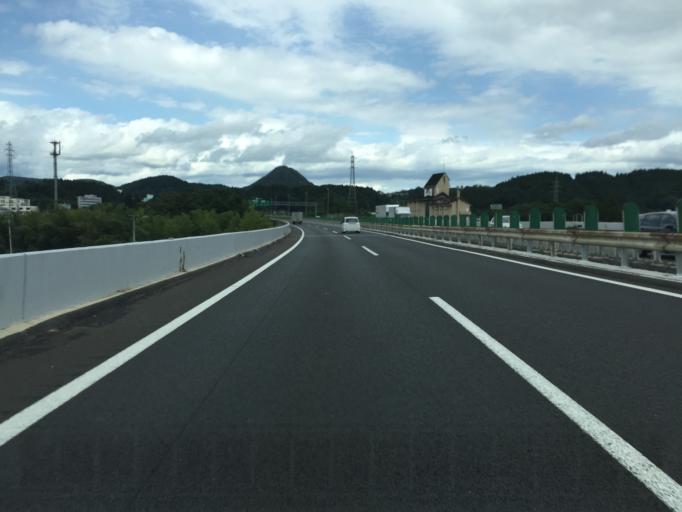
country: JP
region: Miyagi
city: Sendai
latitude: 38.2104
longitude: 140.8048
